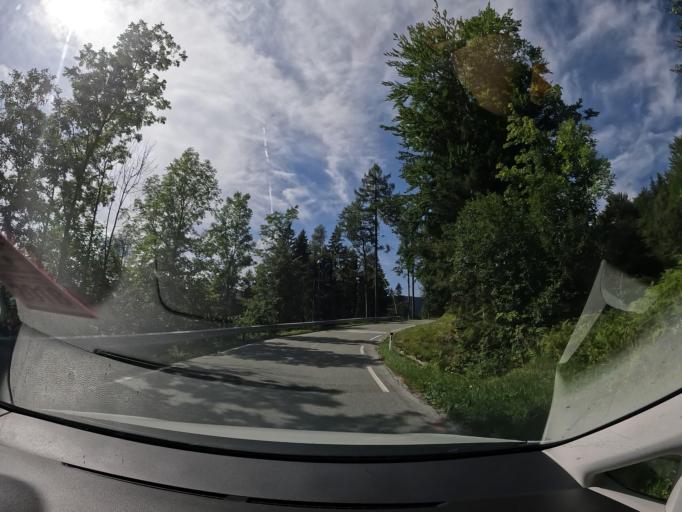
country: AT
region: Carinthia
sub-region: Politischer Bezirk Sankt Veit an der Glan
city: Liebenfels
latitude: 46.7197
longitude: 14.2515
